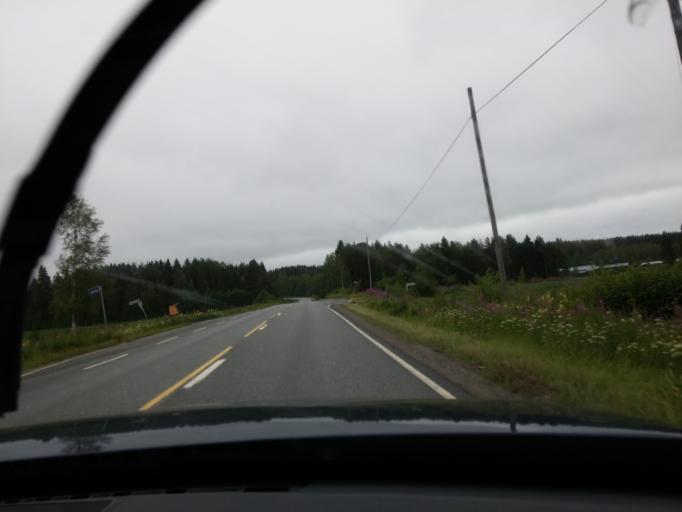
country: FI
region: Central Finland
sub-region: Joutsa
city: Joutsa
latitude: 61.7847
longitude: 26.0500
